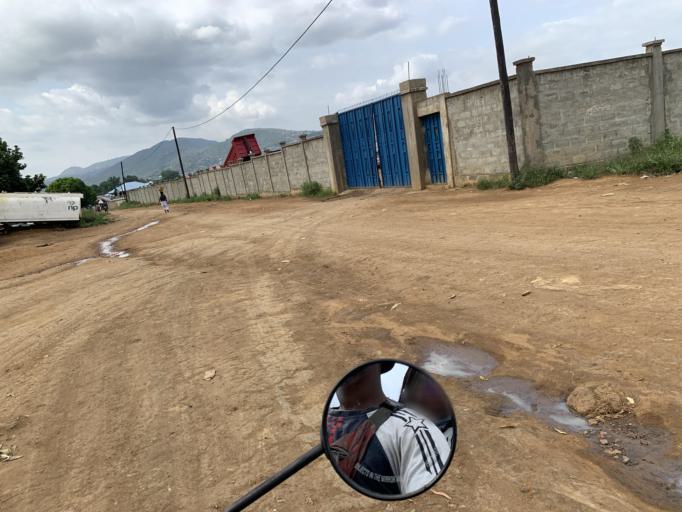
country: SL
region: Western Area
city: Hastings
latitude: 8.3898
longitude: -13.1483
